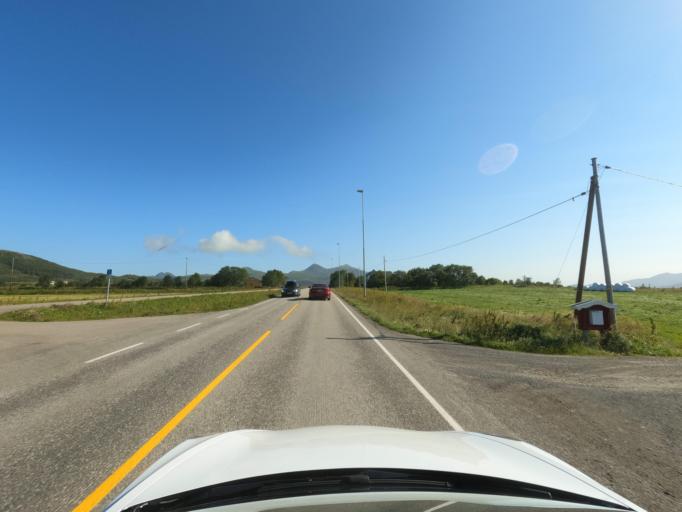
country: NO
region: Nordland
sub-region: Vestvagoy
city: Leknes
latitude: 68.1786
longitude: 13.6286
